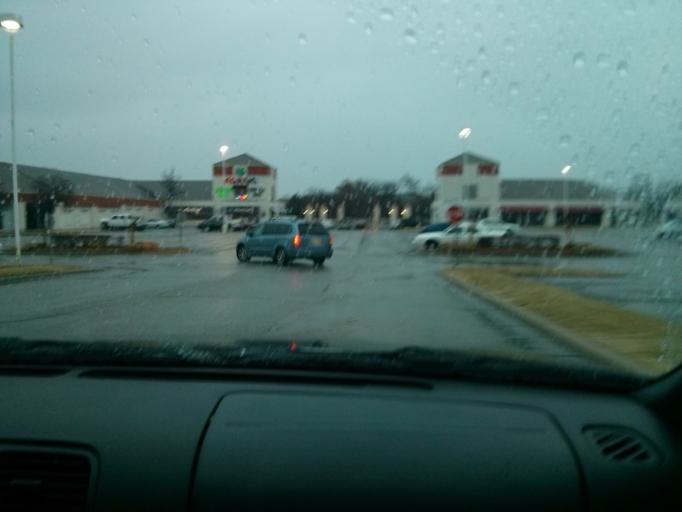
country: US
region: Oklahoma
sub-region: Tulsa County
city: Broken Arrow
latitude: 36.0759
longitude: -95.8841
